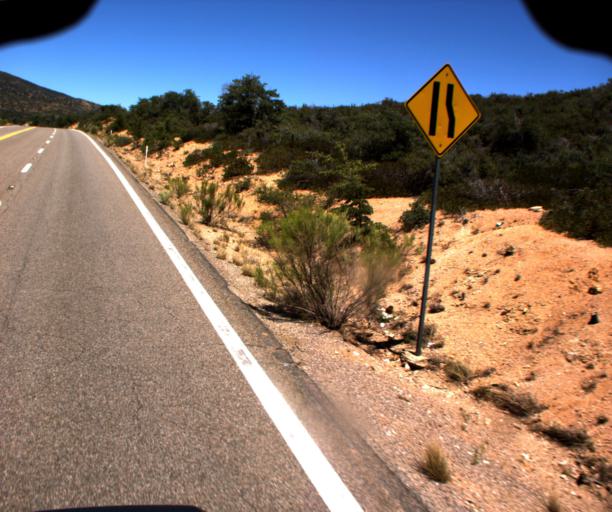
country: US
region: Arizona
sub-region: Gila County
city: Globe
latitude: 33.2397
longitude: -110.7834
